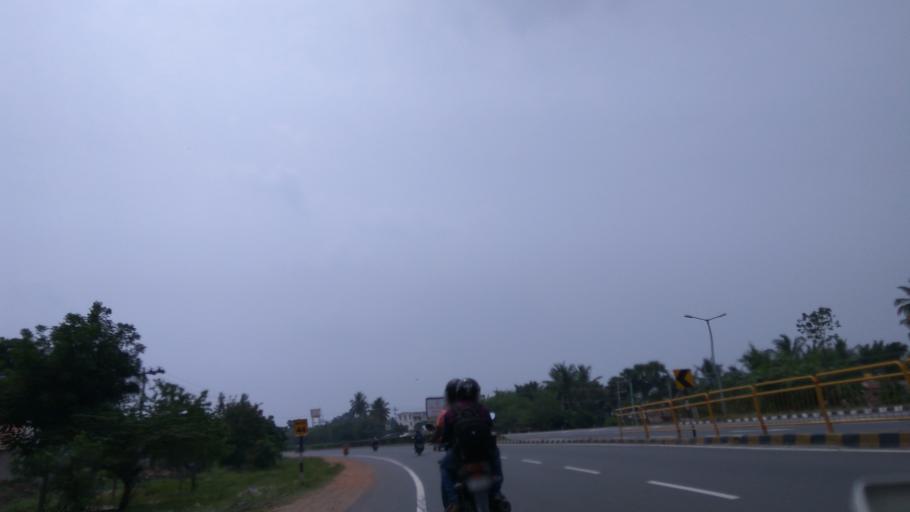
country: IN
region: Tamil Nadu
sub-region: Krishnagiri
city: Kaverippattanam
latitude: 12.2915
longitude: 78.1994
